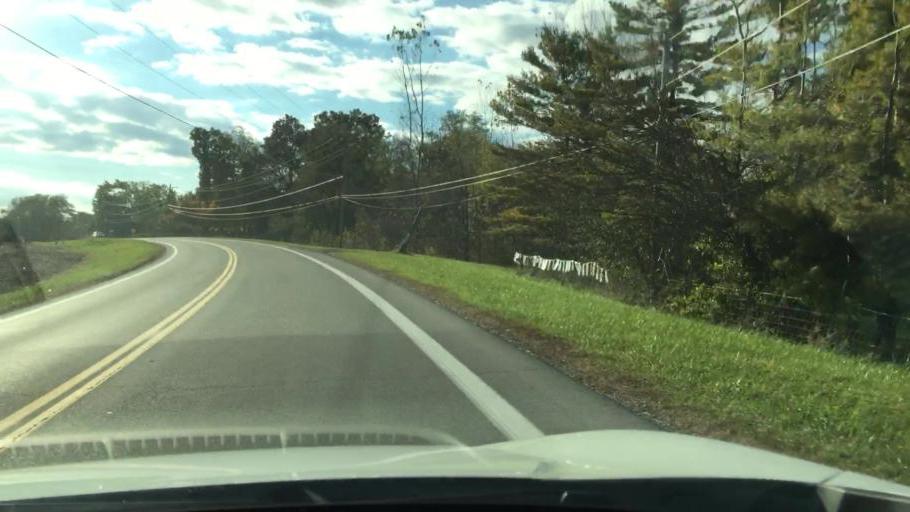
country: US
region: Ohio
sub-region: Champaign County
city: North Lewisburg
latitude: 40.2239
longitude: -83.5446
